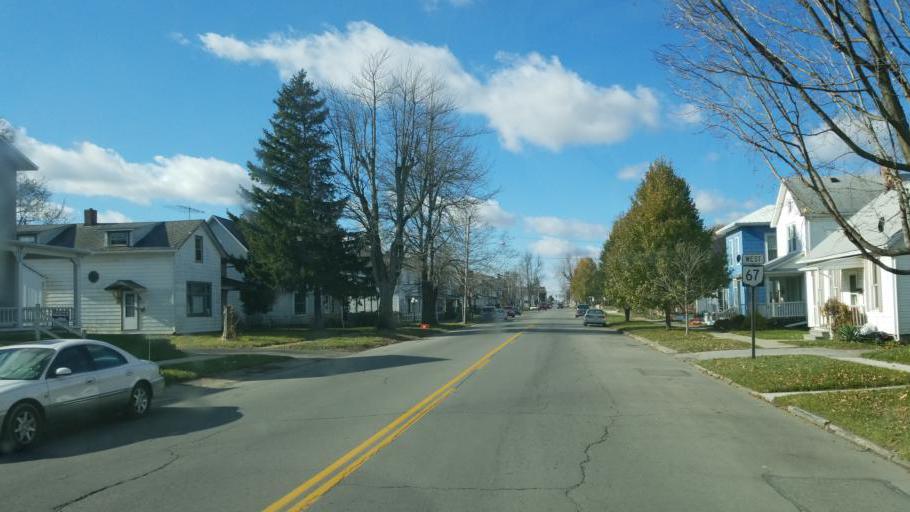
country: US
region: Ohio
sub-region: Hardin County
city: Kenton
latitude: 40.6480
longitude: -83.6025
